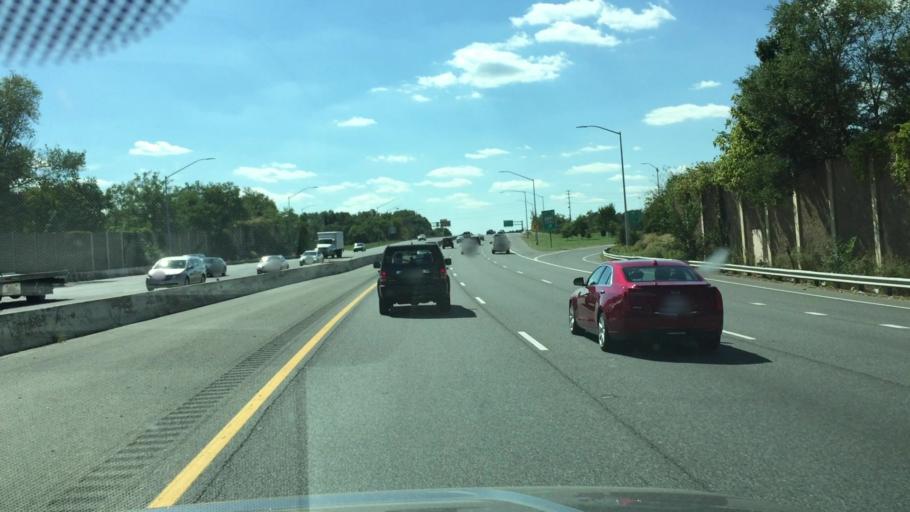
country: US
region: Maryland
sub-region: Anne Arundel County
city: Ferndale
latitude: 39.1797
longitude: -76.6340
